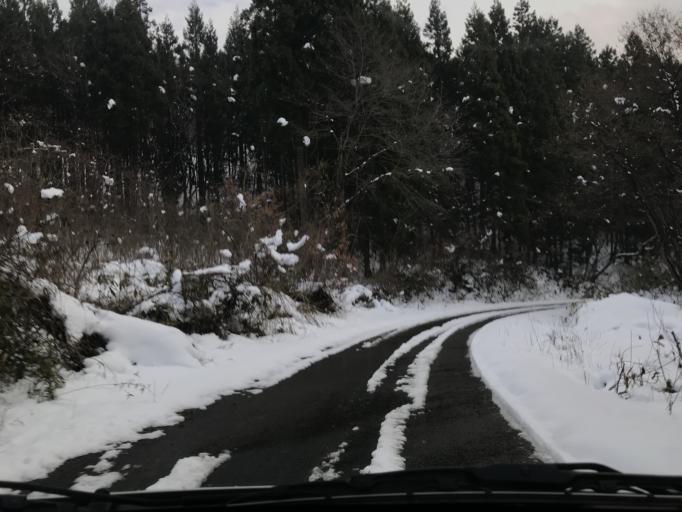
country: JP
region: Iwate
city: Mizusawa
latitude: 39.0517
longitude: 141.0577
